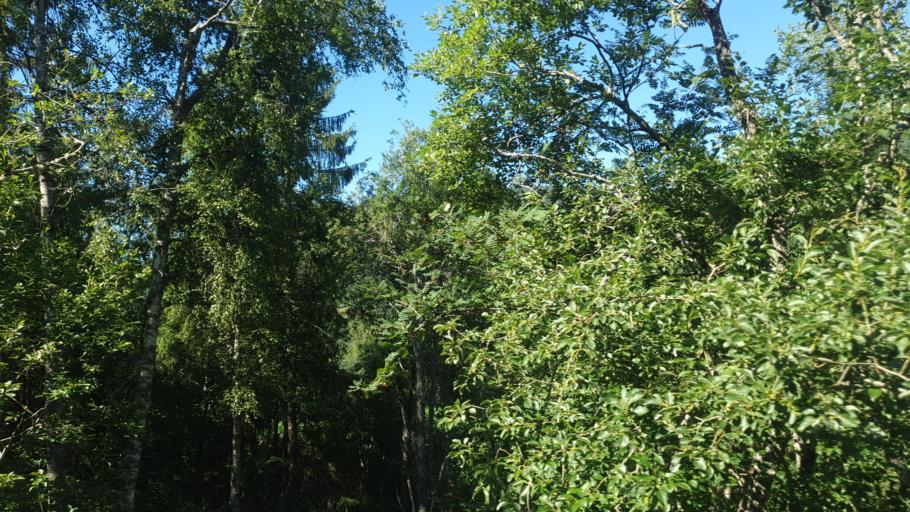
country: NO
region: Sor-Trondelag
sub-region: Meldal
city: Meldal
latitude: 63.1654
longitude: 9.7350
